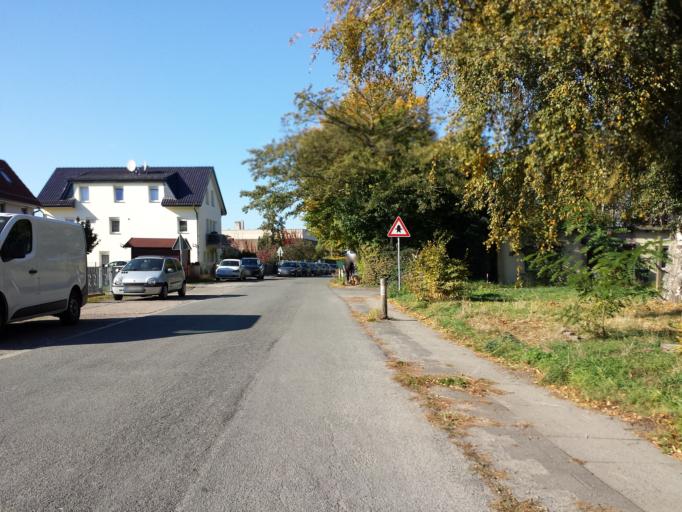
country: DE
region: Lower Saxony
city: Ritterhude
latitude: 53.1388
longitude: 8.7280
